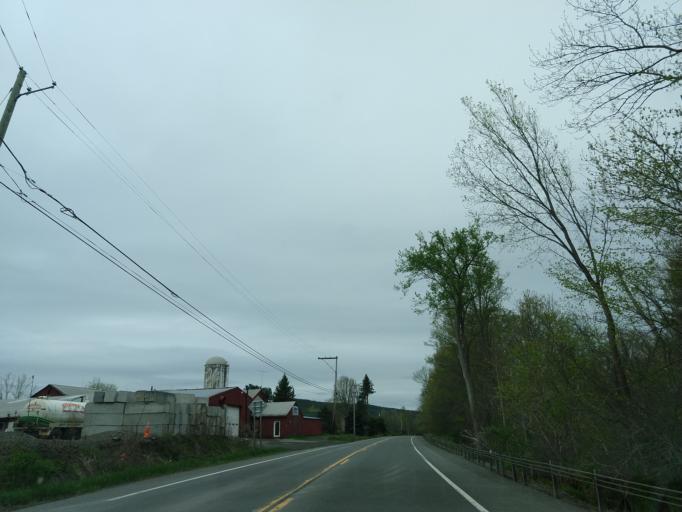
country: US
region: New York
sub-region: Tompkins County
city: Dryden
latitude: 42.4945
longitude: -76.3719
